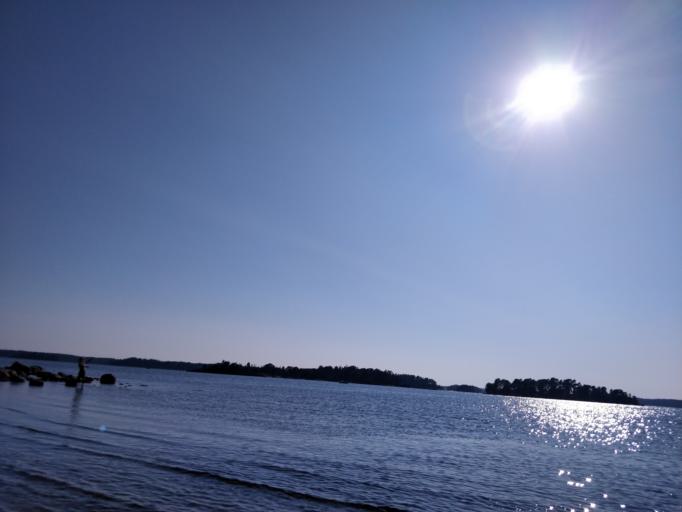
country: FI
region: Uusimaa
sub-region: Helsinki
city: Vantaa
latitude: 60.1851
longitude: 25.1433
